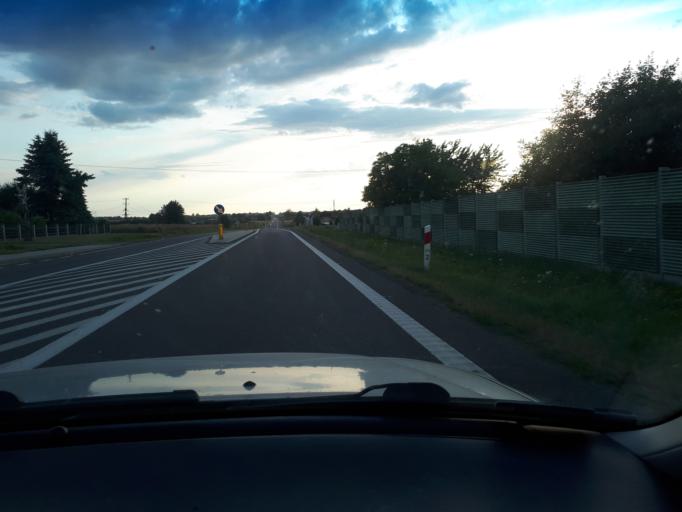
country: PL
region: Subcarpathian Voivodeship
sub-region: Powiat rzeszowski
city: Trzciana
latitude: 50.0715
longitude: 21.8058
